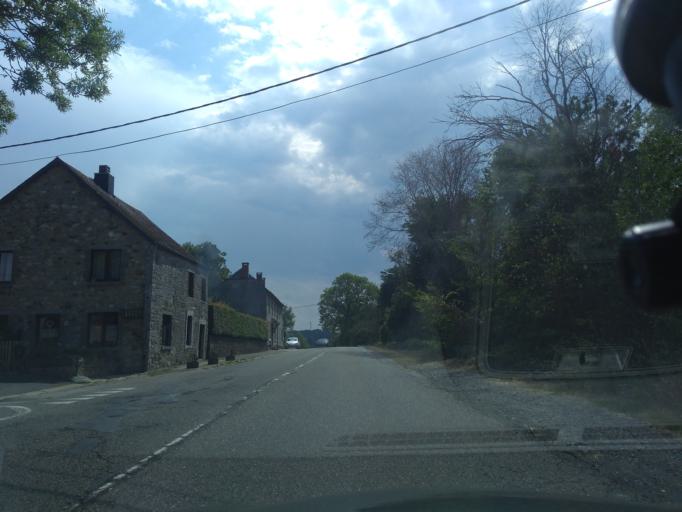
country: BE
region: Wallonia
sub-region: Province de Namur
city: Dinant
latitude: 50.2103
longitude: 4.8982
